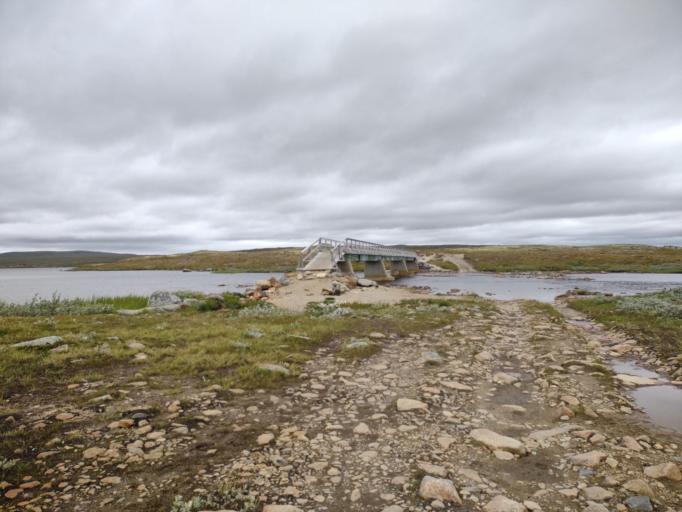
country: NO
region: Hordaland
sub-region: Eidfjord
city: Eidfjord
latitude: 60.2465
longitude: 7.5462
